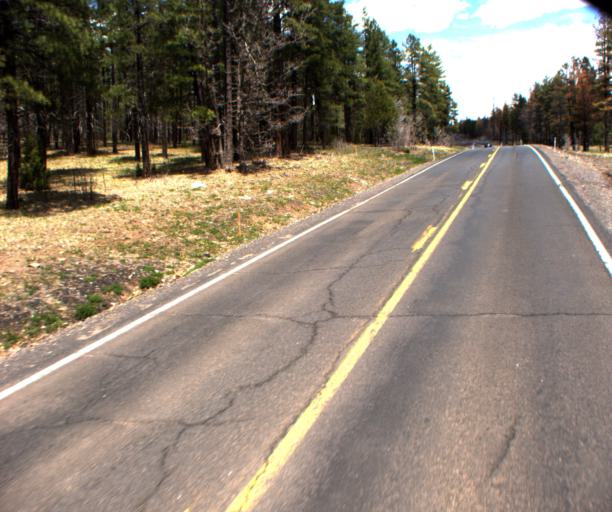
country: US
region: Arizona
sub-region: Coconino County
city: Kachina Village
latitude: 35.0748
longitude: -111.7305
